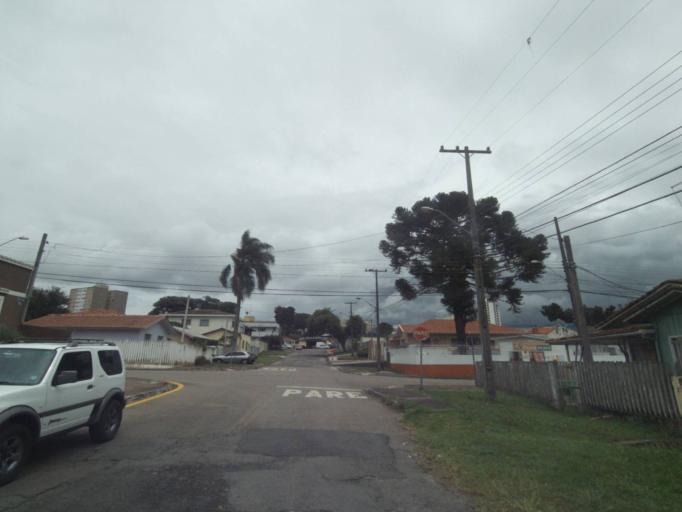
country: BR
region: Parana
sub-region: Curitiba
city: Curitiba
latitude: -25.4874
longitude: -49.2910
